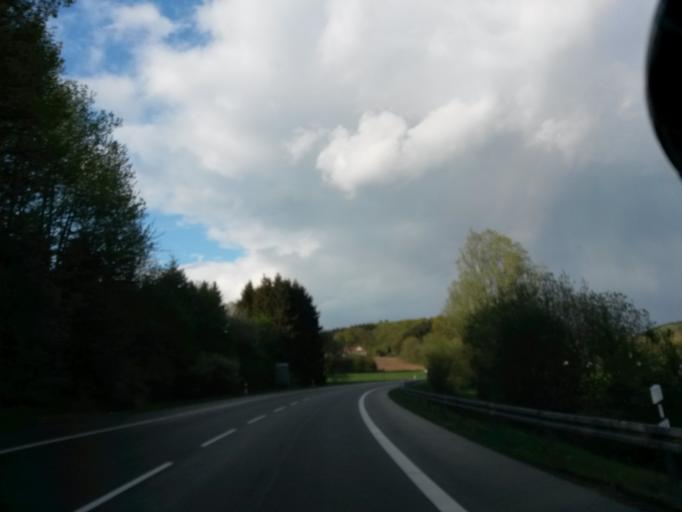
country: DE
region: North Rhine-Westphalia
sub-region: Regierungsbezirk Arnsberg
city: Herscheid
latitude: 51.1128
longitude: 7.7291
